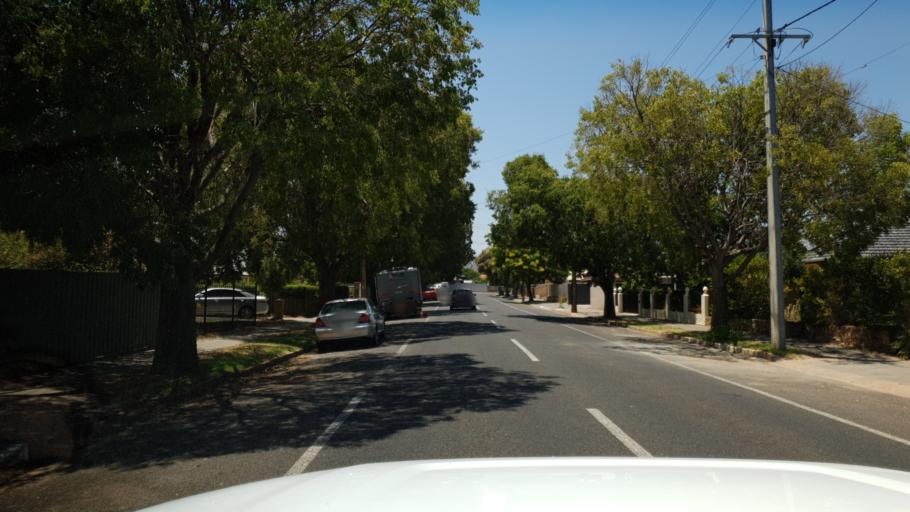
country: AU
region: South Australia
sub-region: Mitcham
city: Clarence Gardens
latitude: -34.9802
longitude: 138.5811
